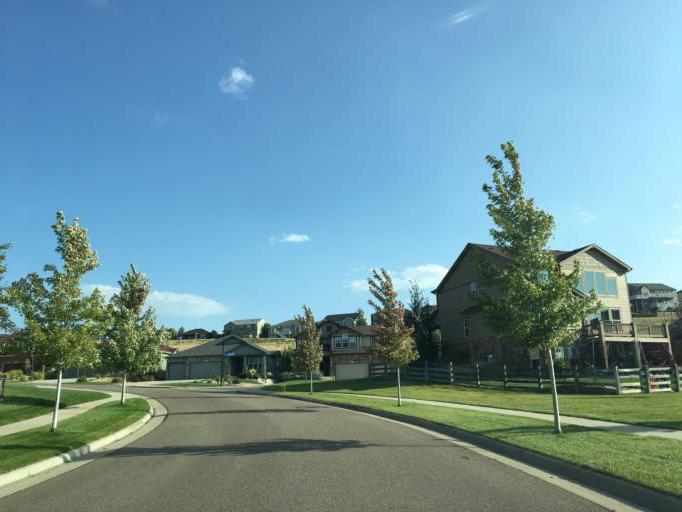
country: US
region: Colorado
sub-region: Jefferson County
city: Arvada
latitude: 39.8538
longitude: -105.1610
